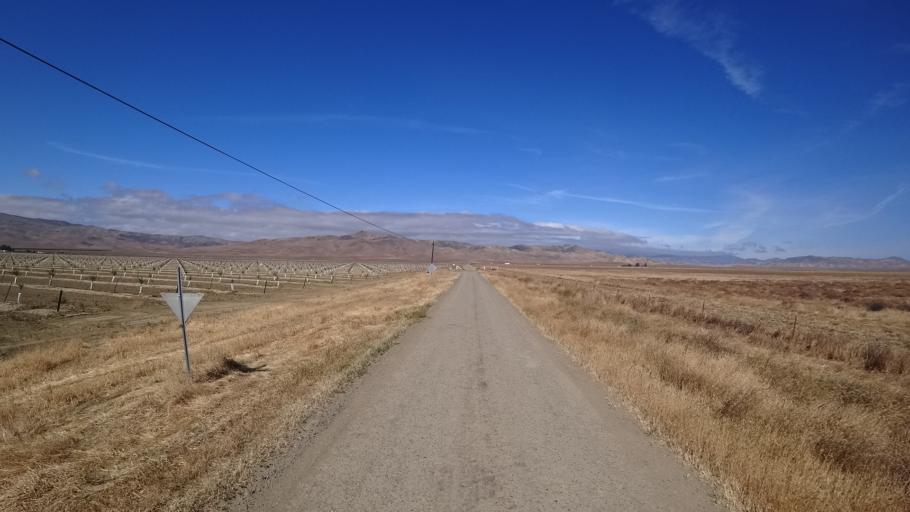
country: US
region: California
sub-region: Kings County
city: Avenal
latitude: 35.8179
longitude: -120.0840
